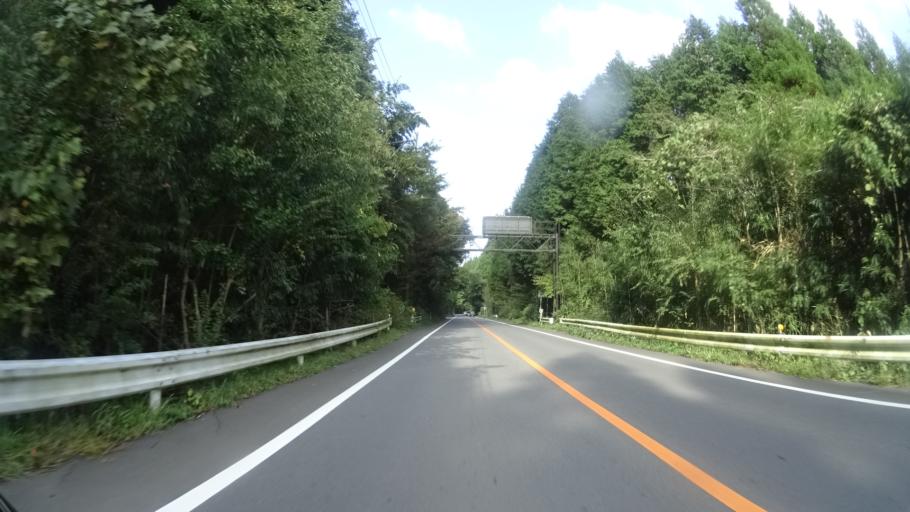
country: JP
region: Kumamoto
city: Aso
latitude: 33.0856
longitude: 131.0665
